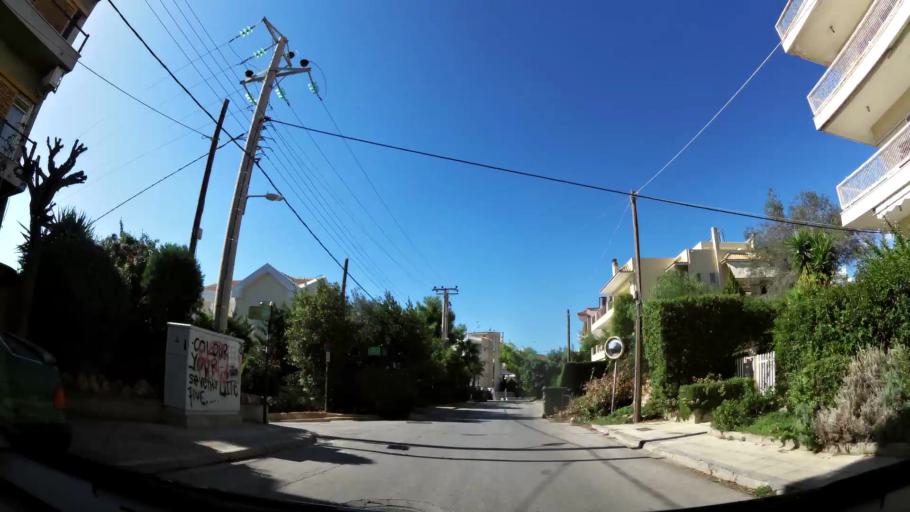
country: GR
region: Attica
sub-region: Nomarchia Anatolikis Attikis
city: Voula
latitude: 37.8349
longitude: 23.7764
